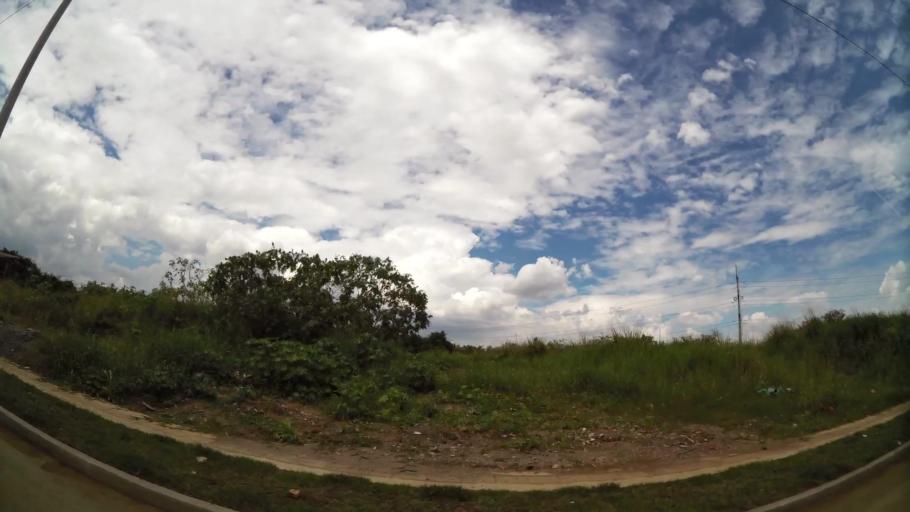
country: CO
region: Valle del Cauca
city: Cali
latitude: 3.3847
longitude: -76.5104
